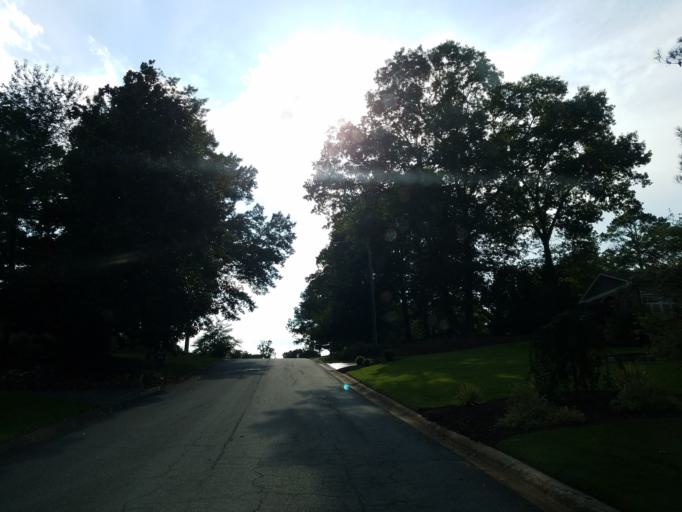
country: US
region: Georgia
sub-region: Fulton County
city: Sandy Springs
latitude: 33.9665
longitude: -84.4411
